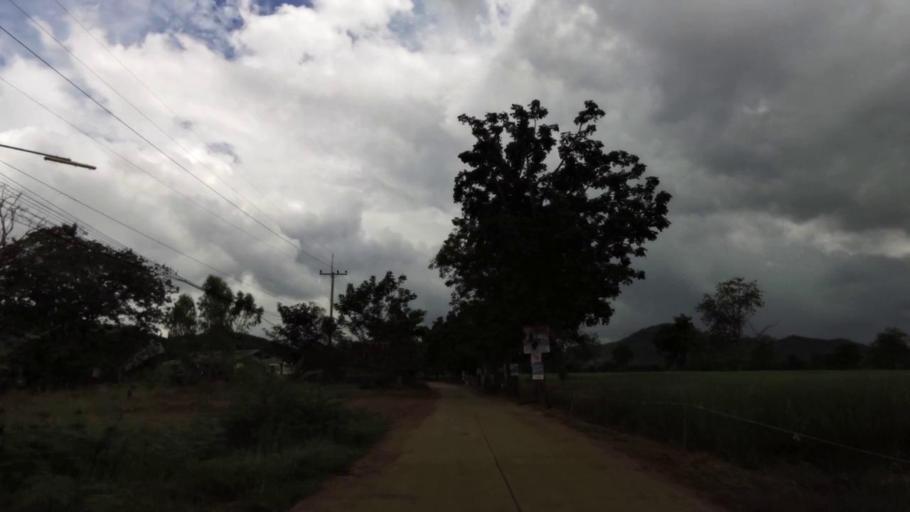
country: TH
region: Nakhon Sawan
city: Phai Sali
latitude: 15.6038
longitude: 100.6703
